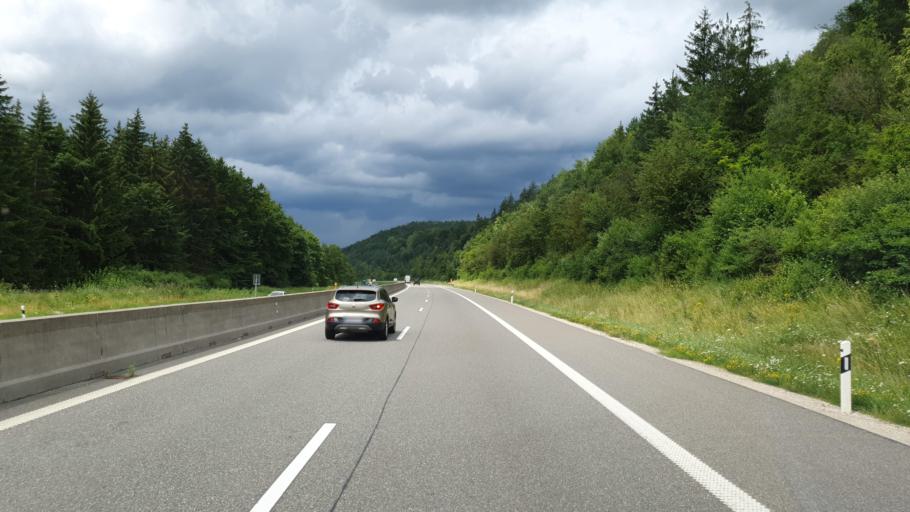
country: DE
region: Baden-Wuerttemberg
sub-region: Freiburg Region
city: Immendingen
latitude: 47.9042
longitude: 8.6986
